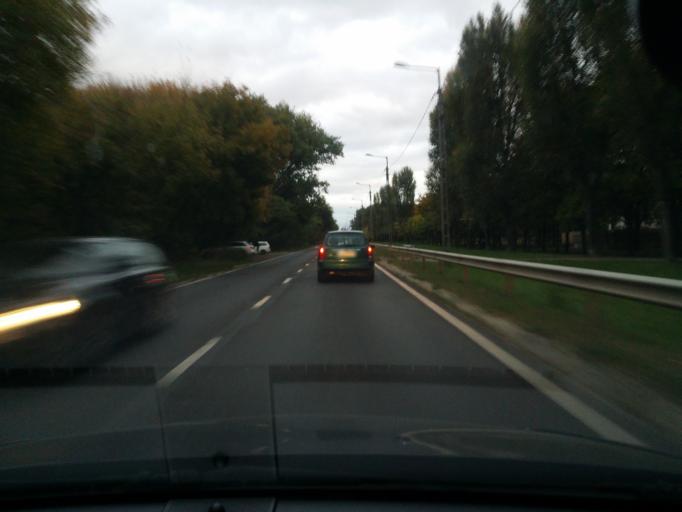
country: HU
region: Budapest
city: Budapest XV. keruelet
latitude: 47.5453
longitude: 19.1461
